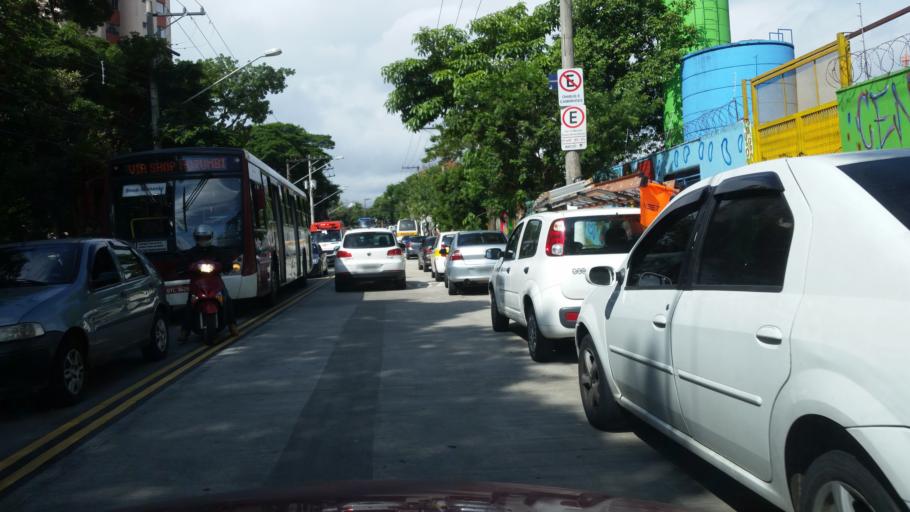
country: BR
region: Sao Paulo
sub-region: Diadema
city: Diadema
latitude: -23.6603
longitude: -46.7075
